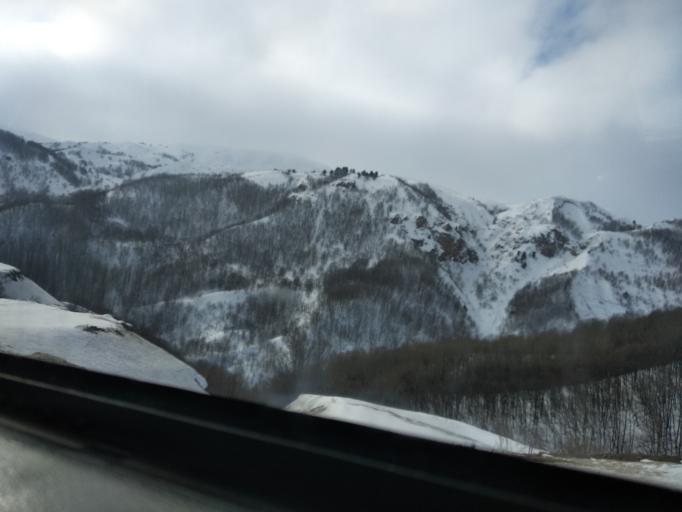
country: TR
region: Erzincan
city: Catalarmut
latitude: 39.8970
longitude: 39.3858
